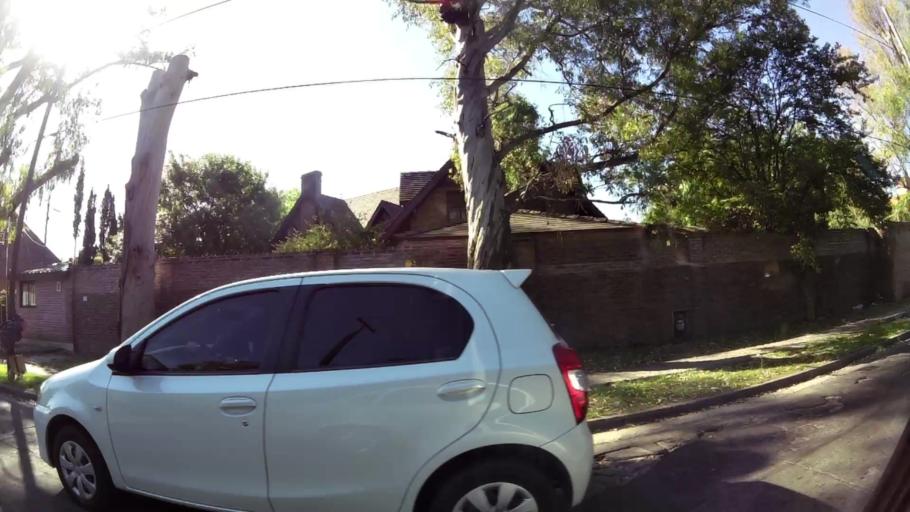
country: AR
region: Buenos Aires
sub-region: Partido de San Isidro
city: San Isidro
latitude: -34.4872
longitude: -58.5545
